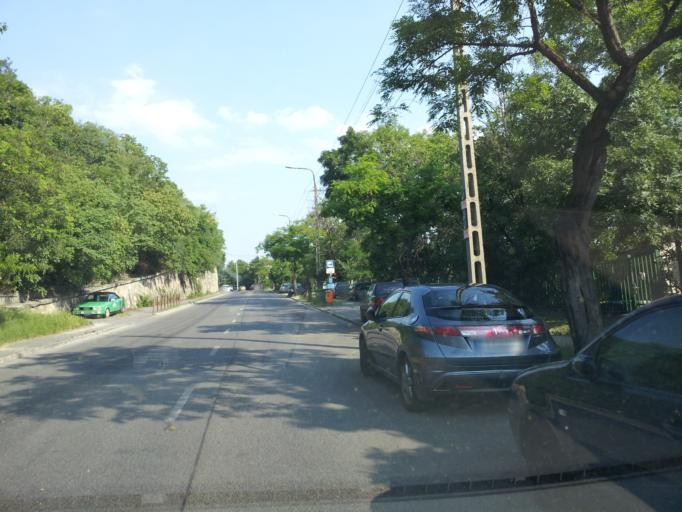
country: HU
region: Budapest
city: Budapest XII. keruelet
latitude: 47.4839
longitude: 19.0210
